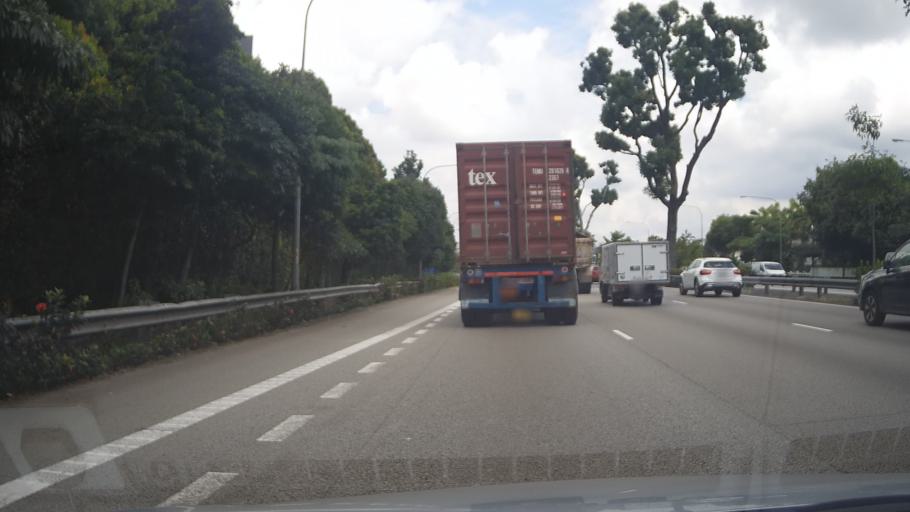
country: SG
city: Singapore
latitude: 1.3192
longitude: 103.7560
